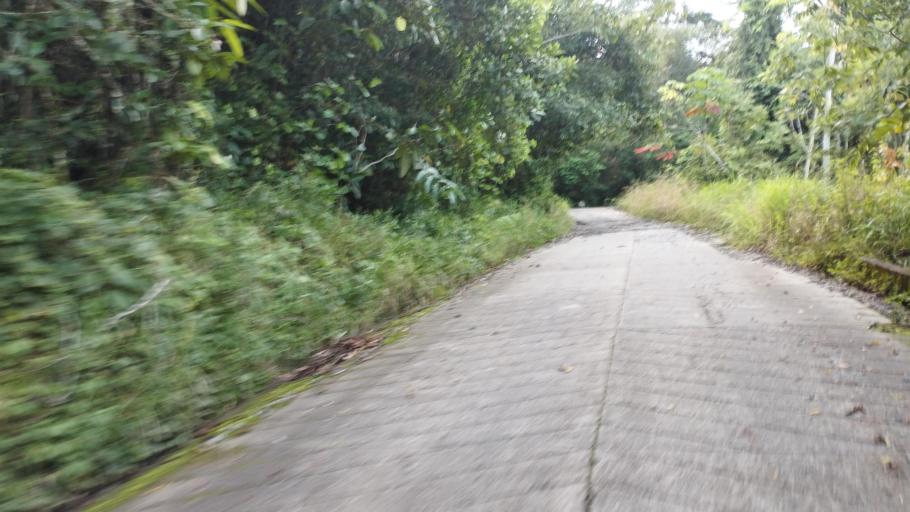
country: CO
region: Boyaca
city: San Luis de Gaceno
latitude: 4.8211
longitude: -73.1004
